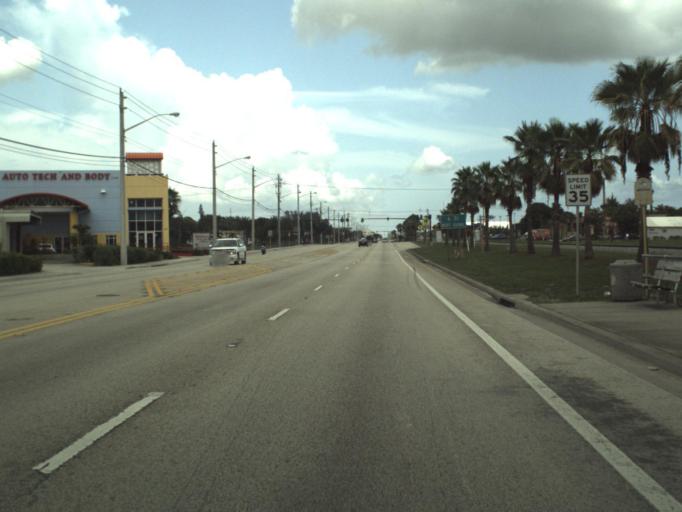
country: US
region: Florida
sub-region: Broward County
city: Pompano Beach
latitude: 26.2348
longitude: -80.1251
